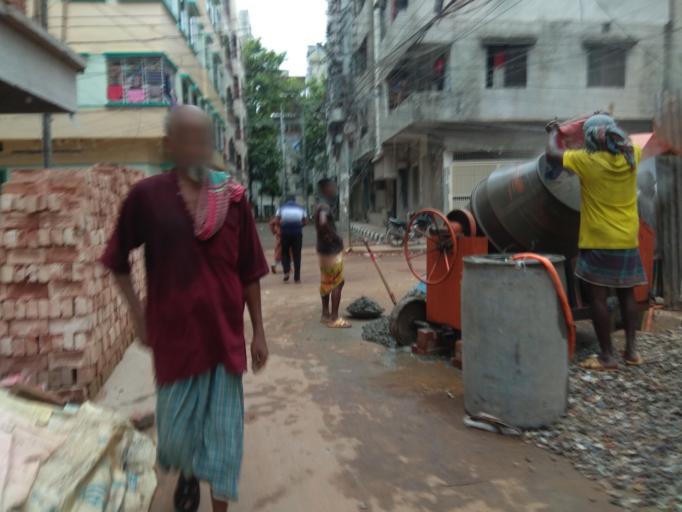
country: BD
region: Dhaka
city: Tungi
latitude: 23.8258
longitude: 90.3745
